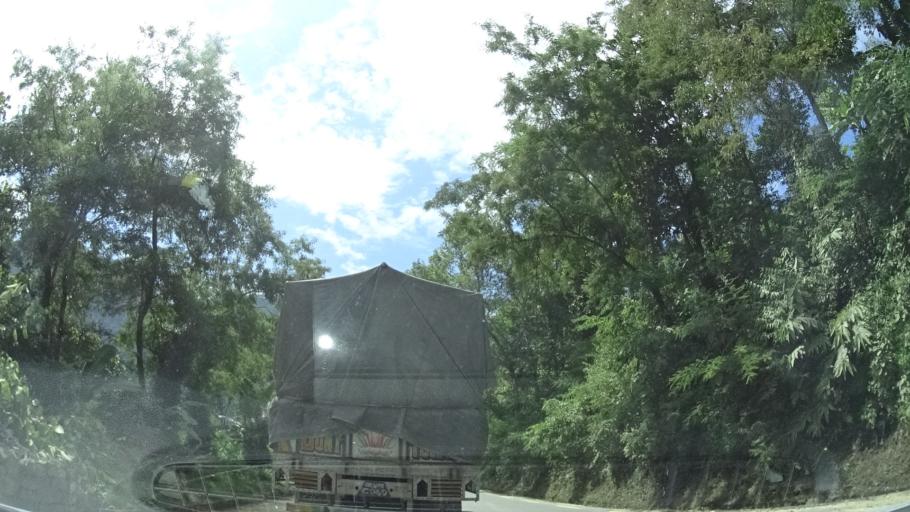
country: NP
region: Central Region
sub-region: Narayani Zone
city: Bharatpur
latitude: 27.8113
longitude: 84.8264
